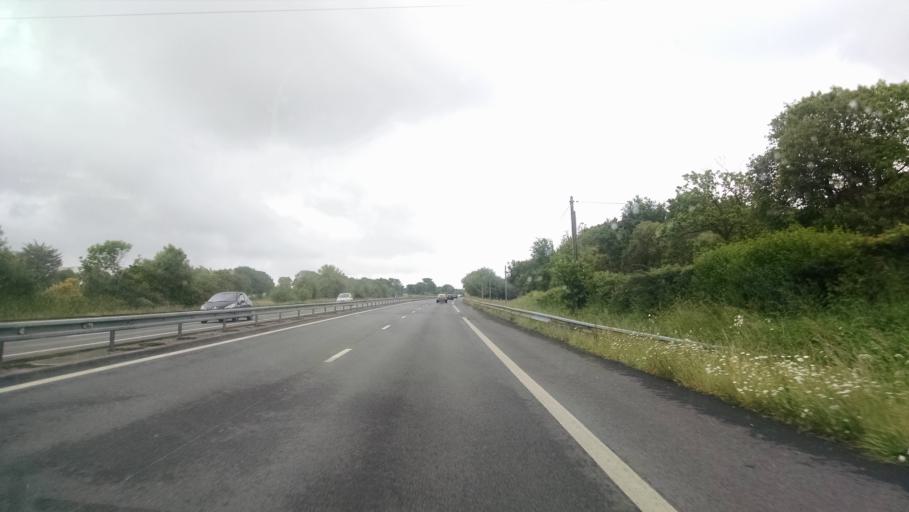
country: FR
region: Brittany
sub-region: Departement du Morbihan
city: Brech
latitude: 47.6991
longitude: -3.0395
